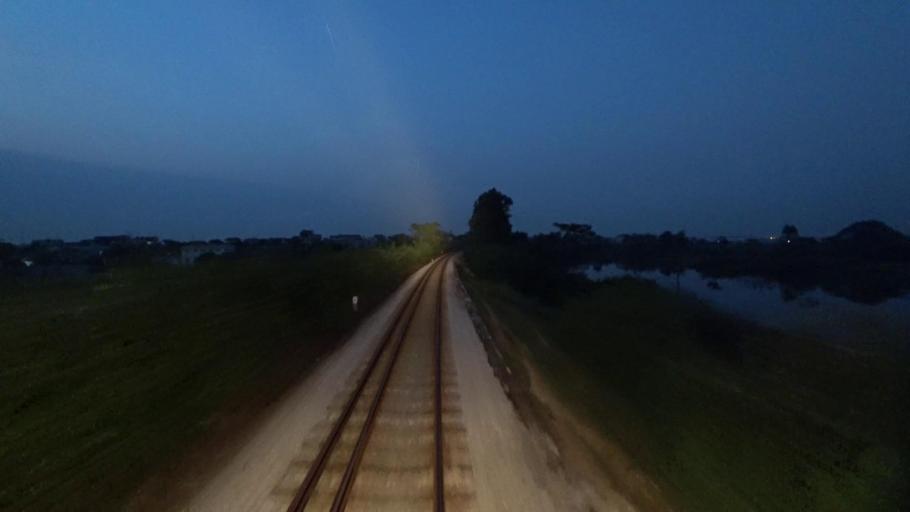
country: VN
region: Ha Noi
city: Soc Son
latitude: 21.2766
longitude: 105.8627
